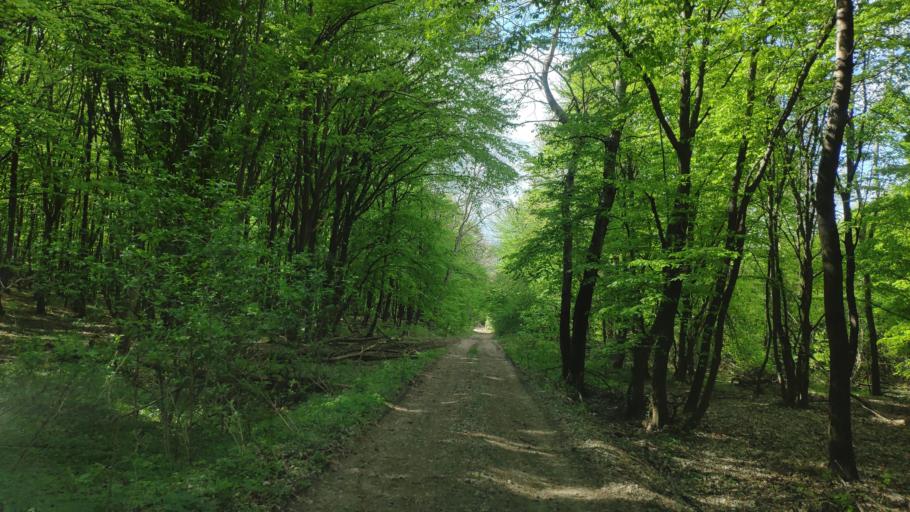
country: SK
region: Kosicky
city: Kosice
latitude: 48.6750
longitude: 21.4476
